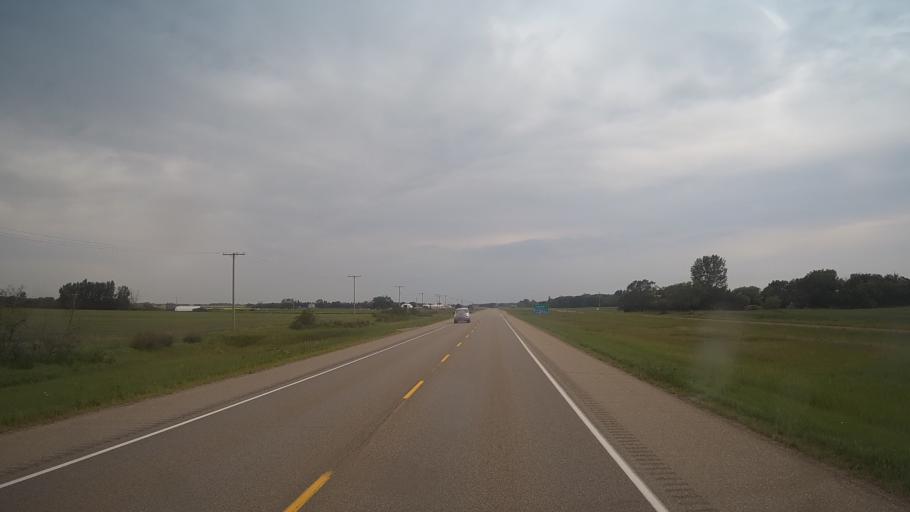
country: CA
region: Saskatchewan
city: Langham
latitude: 52.1289
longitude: -107.2104
